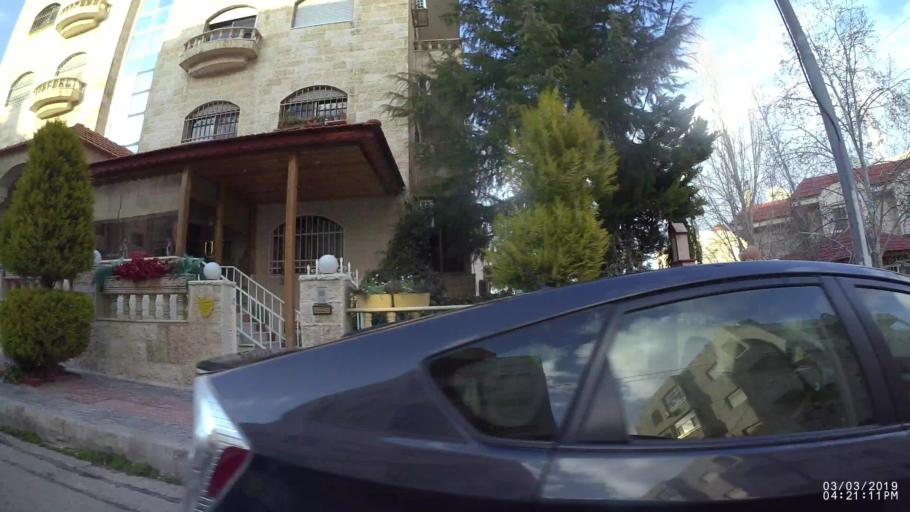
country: JO
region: Amman
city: Al Jubayhah
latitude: 31.9807
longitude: 35.8894
